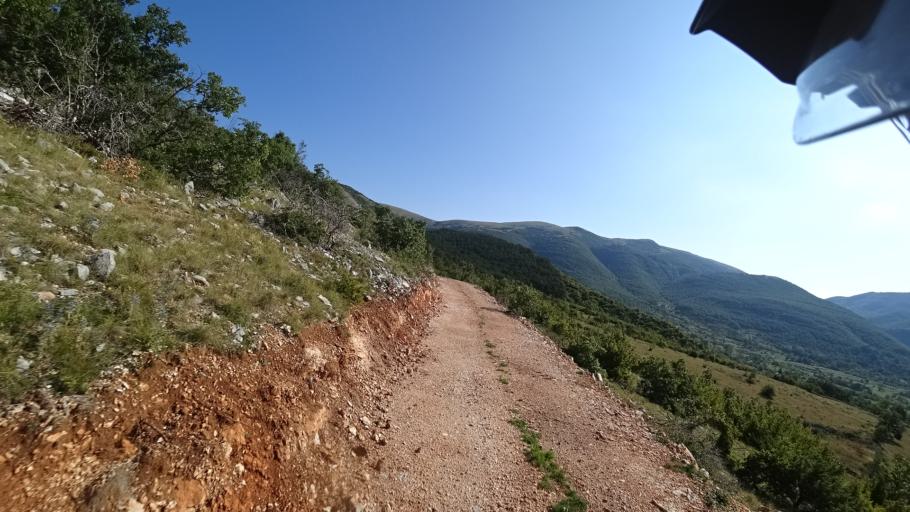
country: HR
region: Sibensko-Kniniska
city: Knin
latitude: 44.1808
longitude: 16.1575
